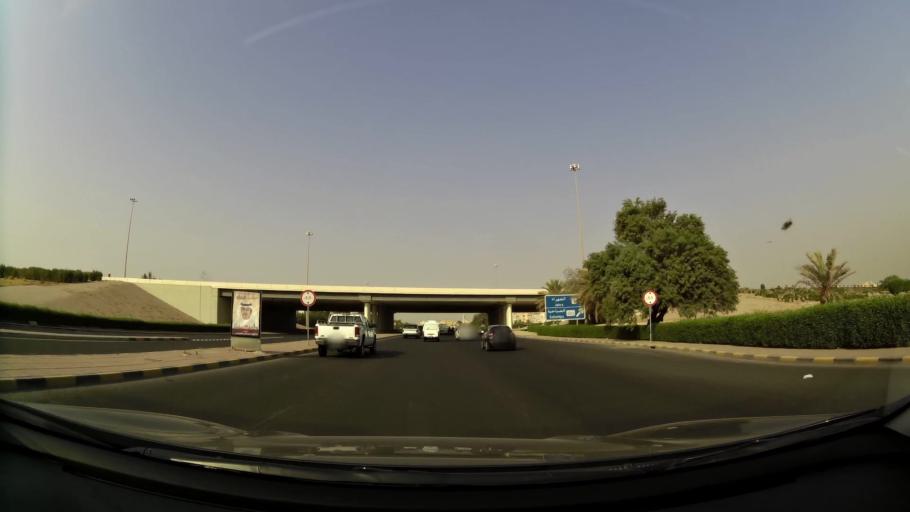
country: KW
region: Mubarak al Kabir
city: Mubarak al Kabir
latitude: 29.1803
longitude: 48.0920
